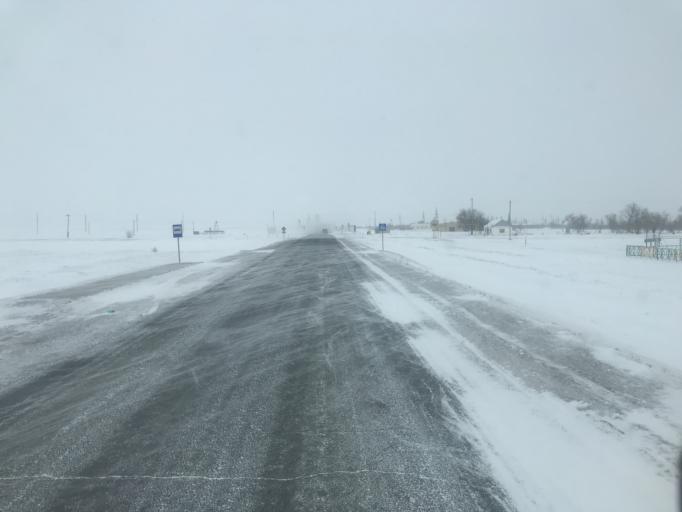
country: KZ
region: Batys Qazaqstan
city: Chapaev
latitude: 50.5123
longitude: 51.0574
